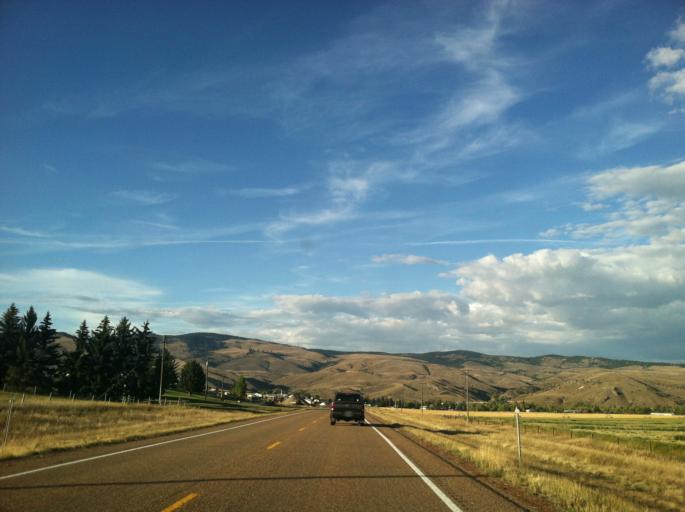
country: US
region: Montana
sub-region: Granite County
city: Philipsburg
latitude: 46.6505
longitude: -113.1619
